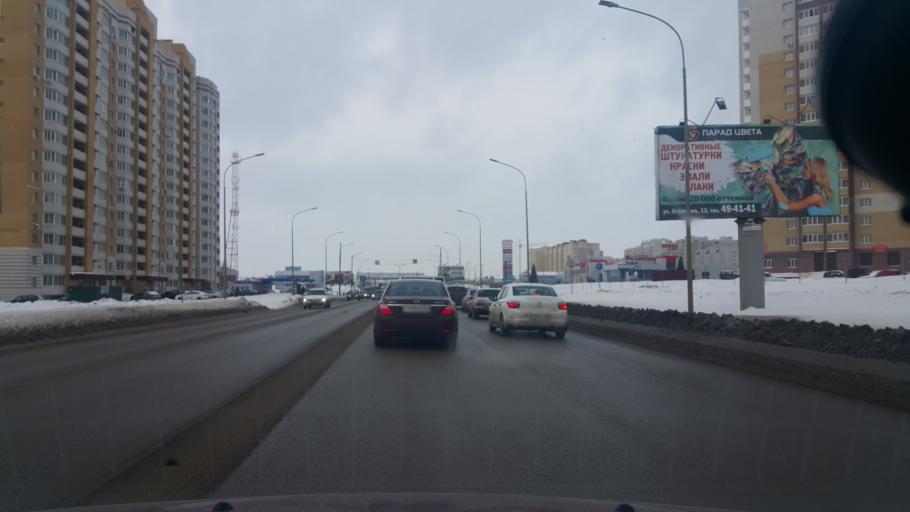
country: RU
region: Tambov
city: Tambov
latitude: 52.7634
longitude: 41.3989
